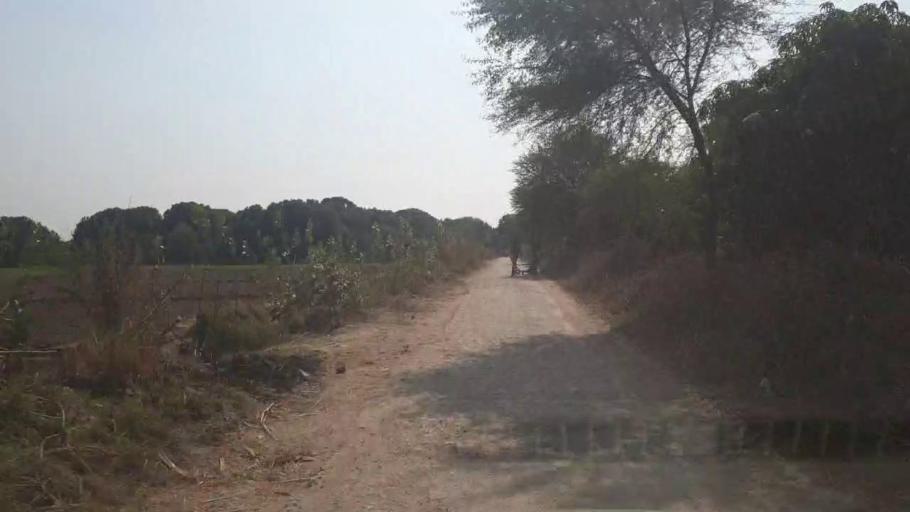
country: PK
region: Sindh
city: Tando Allahyar
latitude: 25.4842
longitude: 68.8480
